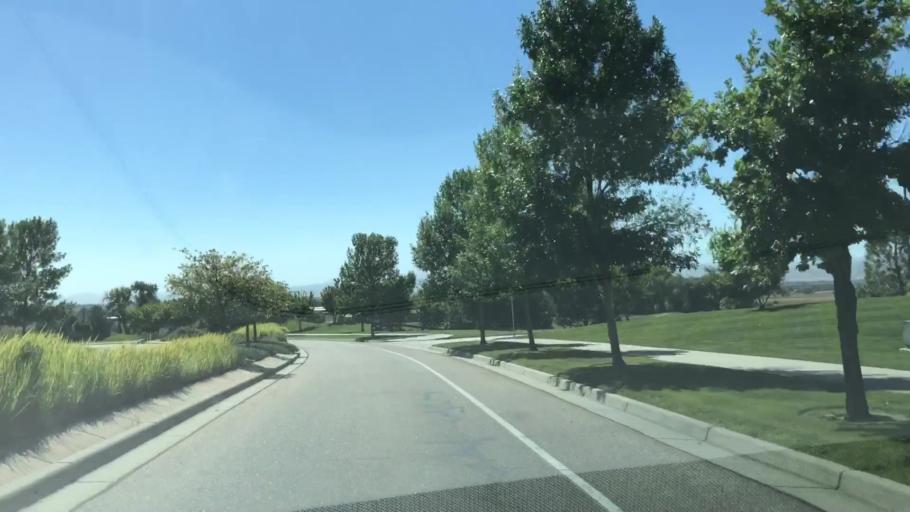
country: US
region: Colorado
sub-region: Weld County
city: Windsor
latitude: 40.5276
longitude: -104.9521
